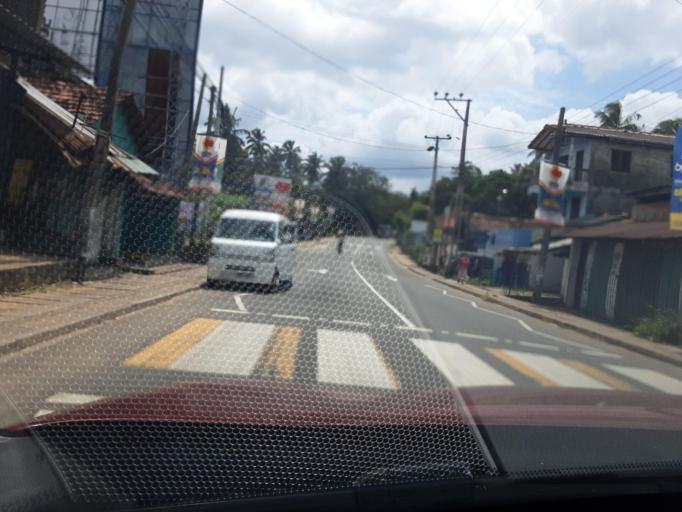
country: LK
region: North Western
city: Kuliyapitiya
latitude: 7.4513
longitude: 80.1919
